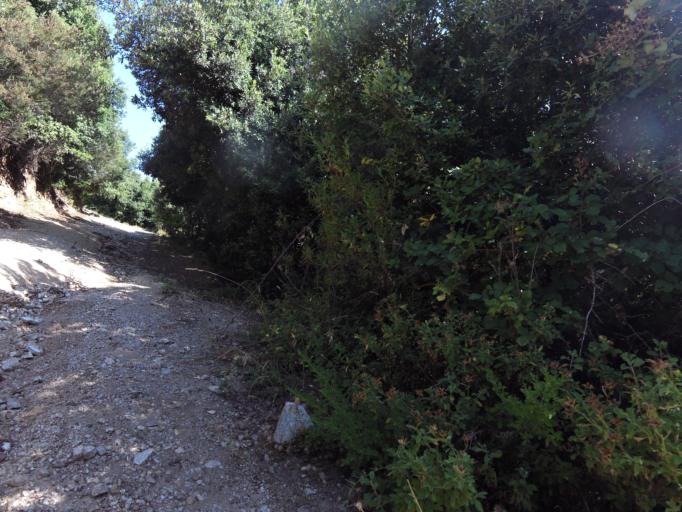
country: IT
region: Calabria
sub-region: Provincia di Reggio Calabria
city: Bivongi
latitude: 38.5051
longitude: 16.4382
